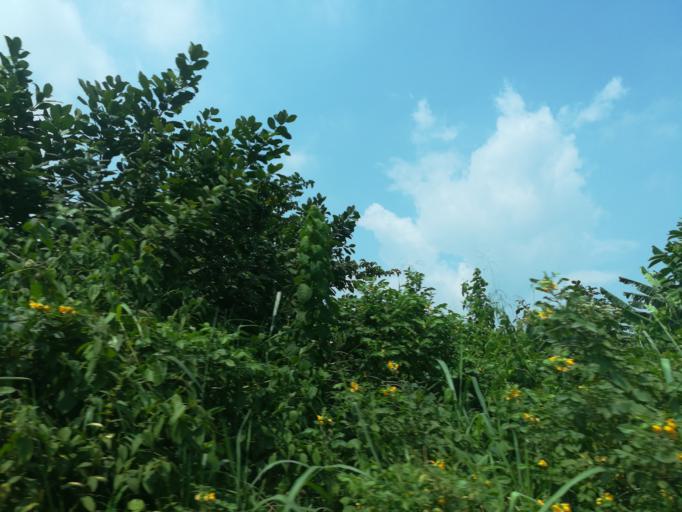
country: NG
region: Lagos
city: Ikorodu
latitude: 6.5968
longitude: 3.6320
